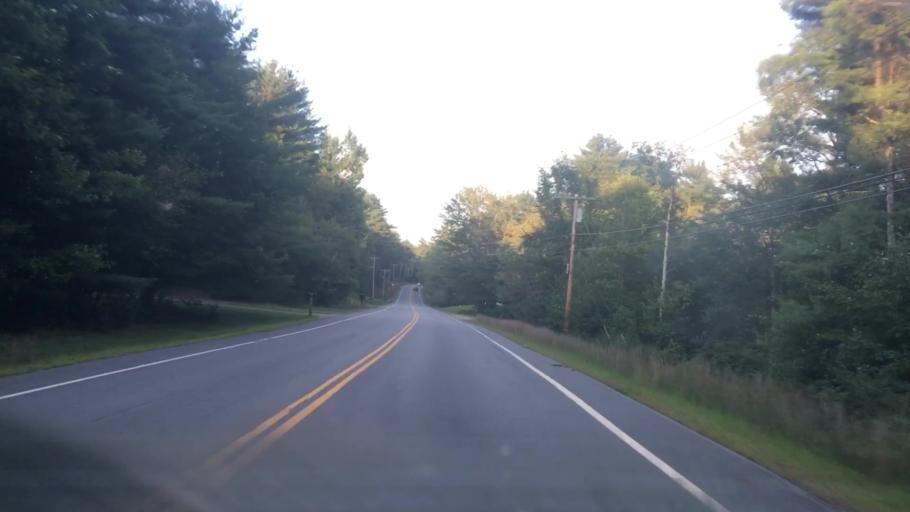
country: US
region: New Hampshire
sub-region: Belknap County
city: Gilmanton
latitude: 43.4265
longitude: -71.3541
